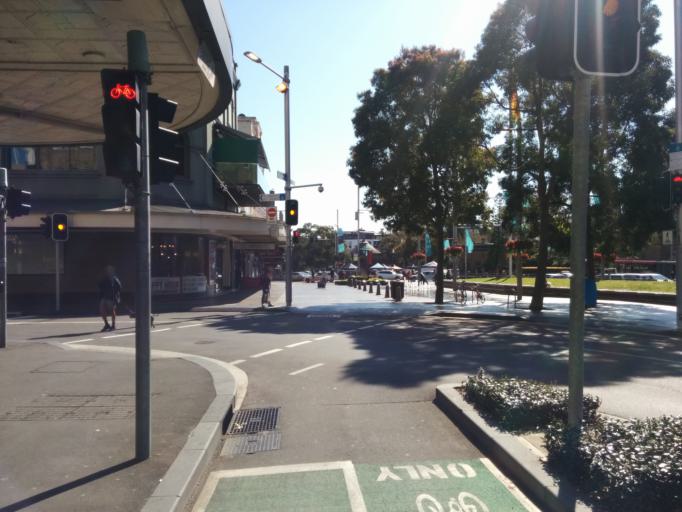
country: AU
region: New South Wales
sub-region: City of Sydney
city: Darlinghurst
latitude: -33.8832
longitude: 151.2163
